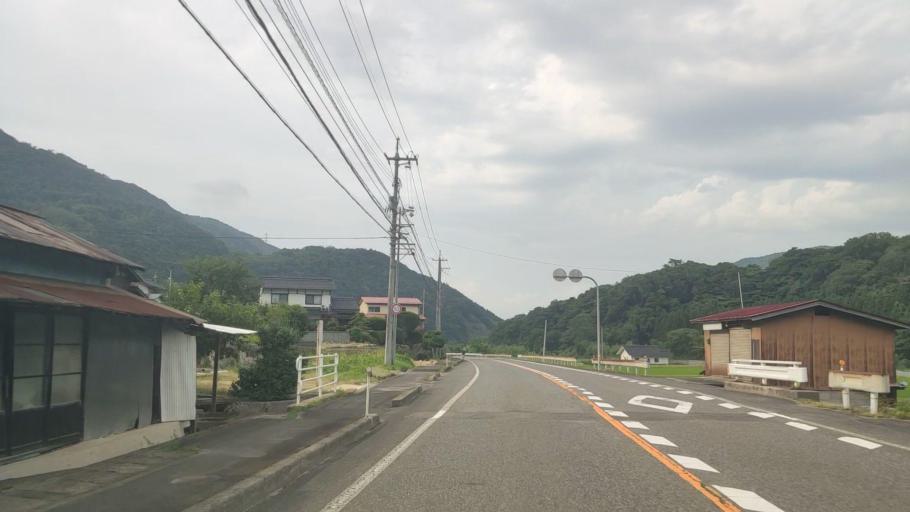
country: JP
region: Tottori
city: Kurayoshi
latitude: 35.3566
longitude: 133.8458
